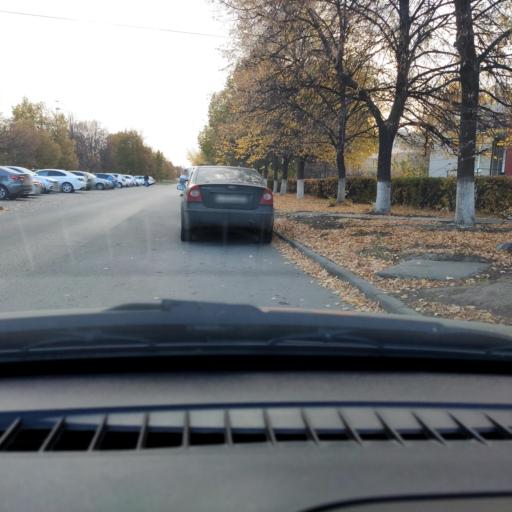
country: RU
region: Samara
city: Tol'yatti
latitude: 53.5256
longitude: 49.3152
